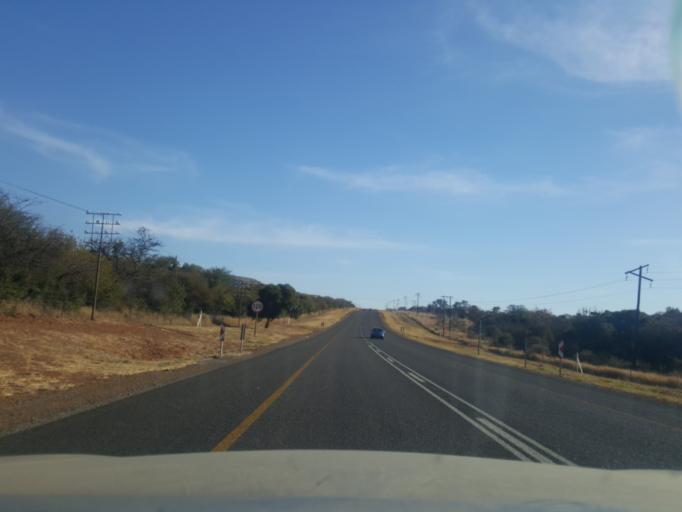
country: ZA
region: North-West
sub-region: Ngaka Modiri Molema District Municipality
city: Zeerust
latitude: -25.5217
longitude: 26.1587
